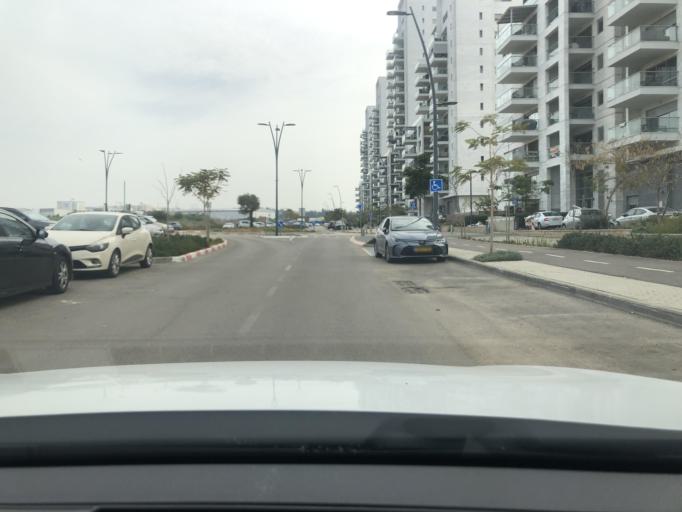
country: IL
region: Central District
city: Rosh Ha'Ayin
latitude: 32.1077
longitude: 34.9452
